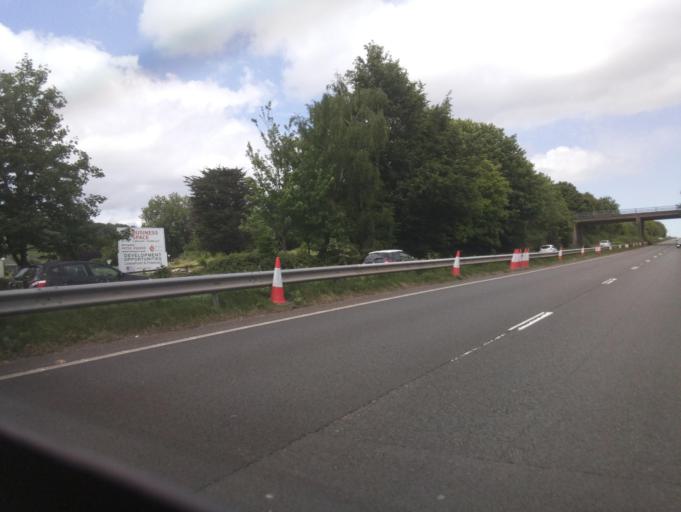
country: GB
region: England
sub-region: Devon
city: Ashburton
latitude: 50.5197
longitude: -3.7446
